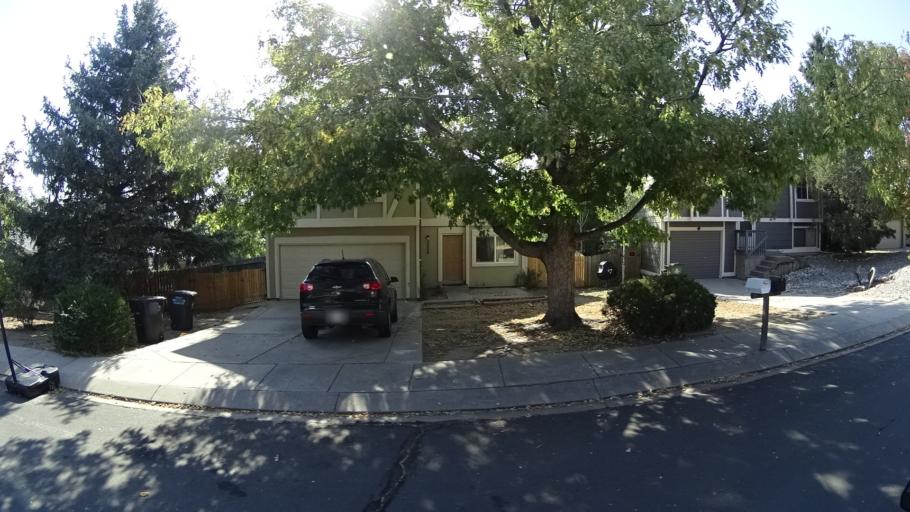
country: US
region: Colorado
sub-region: El Paso County
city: Cimarron Hills
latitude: 38.8791
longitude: -104.7251
